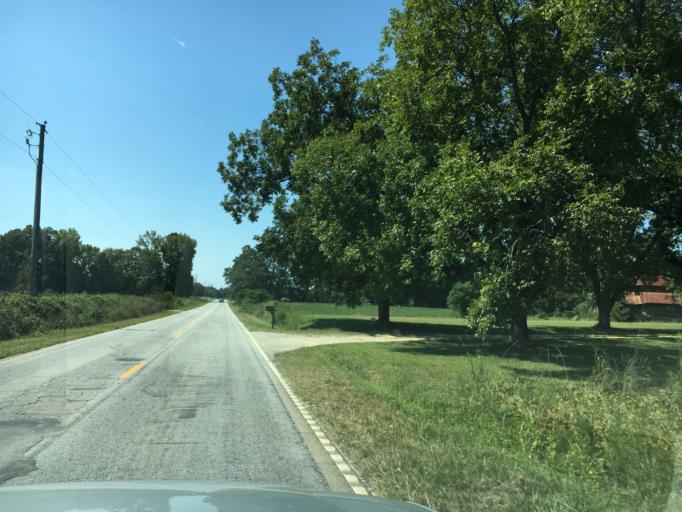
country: US
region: South Carolina
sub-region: Laurens County
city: Joanna
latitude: 34.3893
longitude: -81.8549
